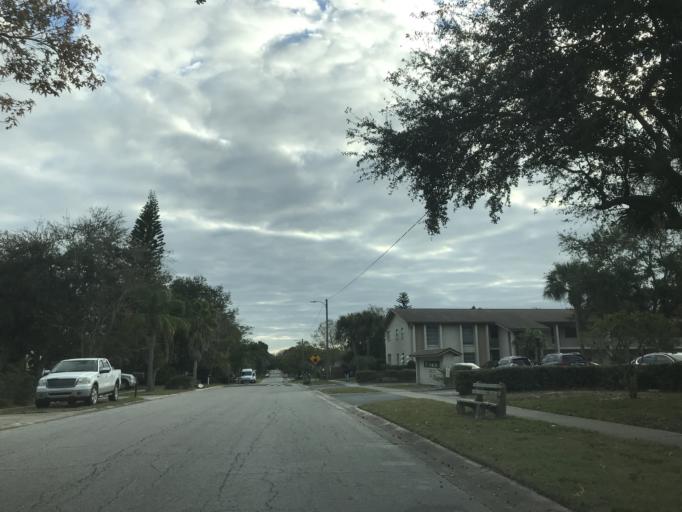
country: US
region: Florida
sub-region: Pinellas County
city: Clearwater
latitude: 27.9535
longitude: -82.7854
